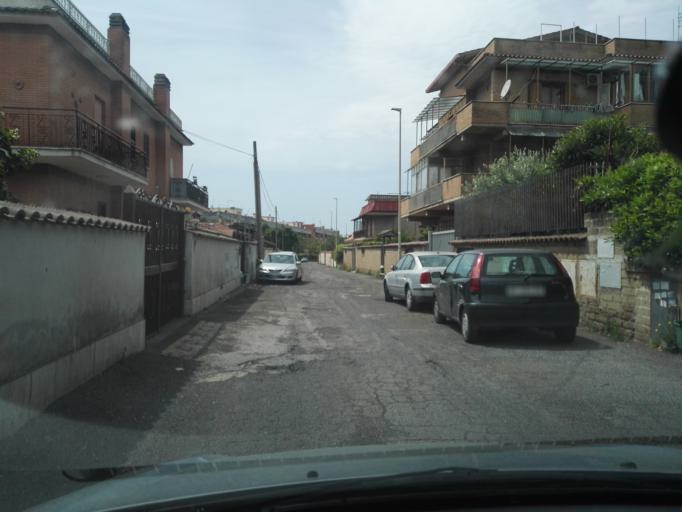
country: IT
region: Latium
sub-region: Citta metropolitana di Roma Capitale
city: Selcetta
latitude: 41.7708
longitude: 12.4809
